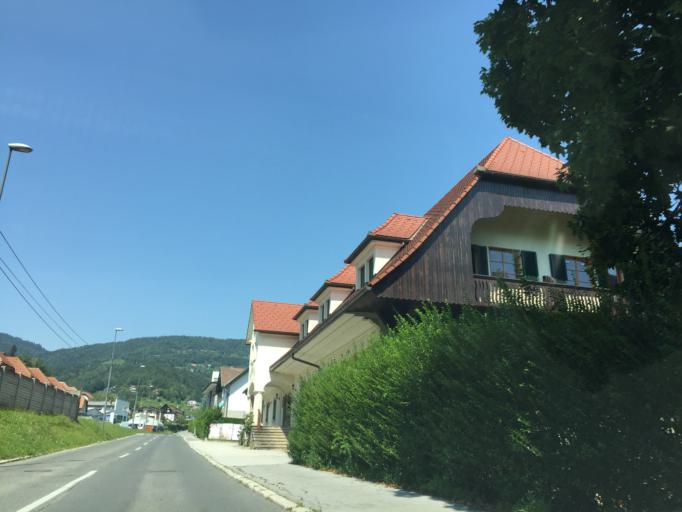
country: SI
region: Trbovlje
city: Trbovlje
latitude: 46.1650
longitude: 15.0517
